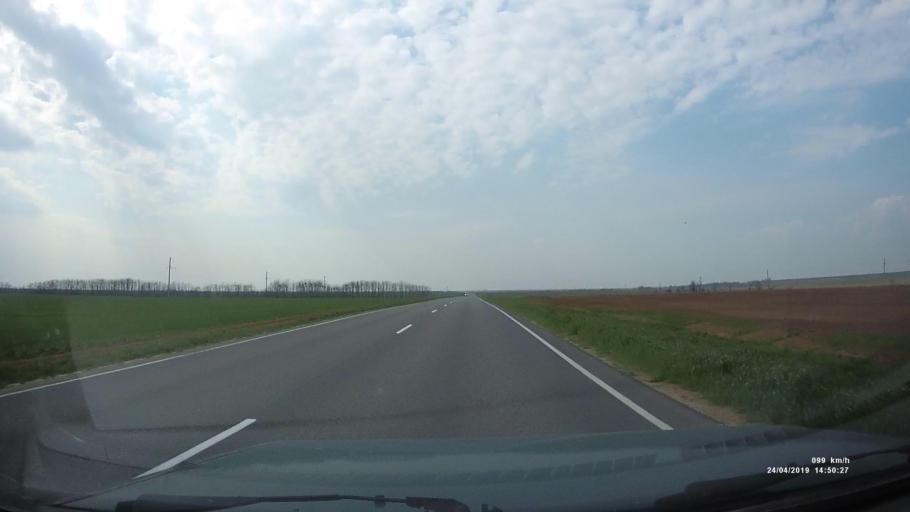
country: RU
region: Rostov
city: Remontnoye
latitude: 46.5173
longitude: 43.7194
